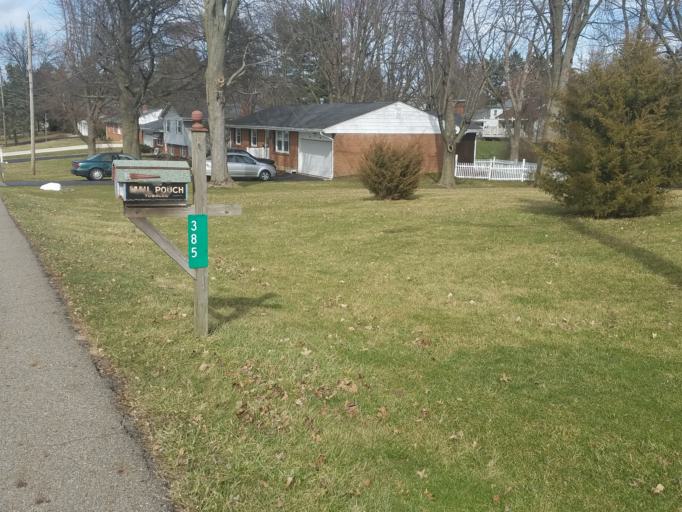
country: US
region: Ohio
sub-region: Morrow County
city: Mount Gilead
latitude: 40.5536
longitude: -82.8383
